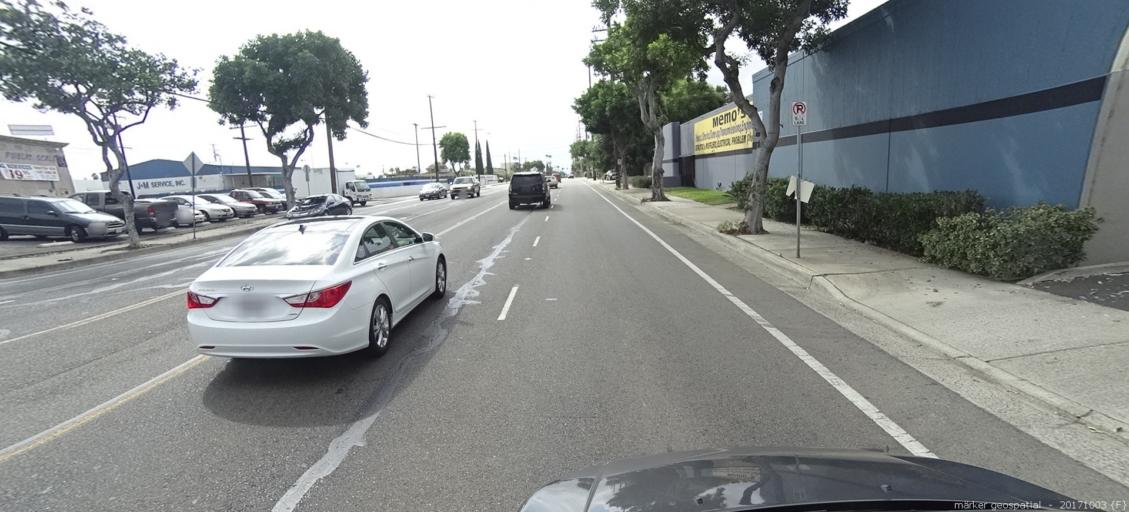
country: US
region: California
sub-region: Orange County
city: Garden Grove
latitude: 33.7634
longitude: -117.9291
